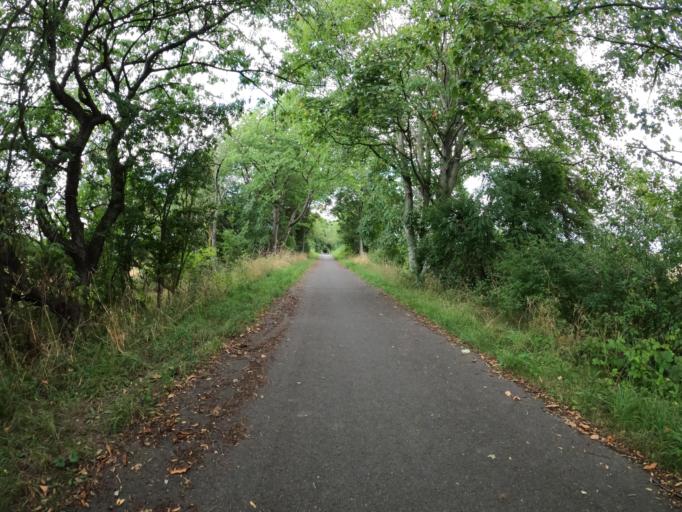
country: DE
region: Mecklenburg-Vorpommern
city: Woldegk
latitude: 53.3746
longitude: 13.5885
